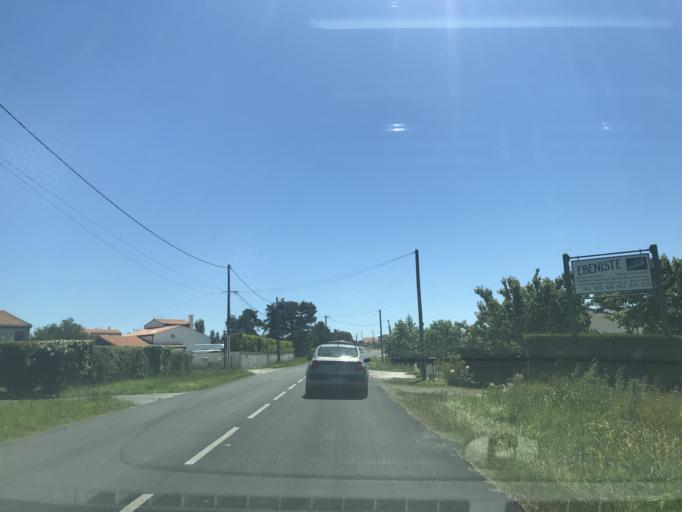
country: FR
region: Poitou-Charentes
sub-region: Departement de la Charente-Maritime
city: Meschers-sur-Gironde
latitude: 45.5788
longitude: -0.9597
